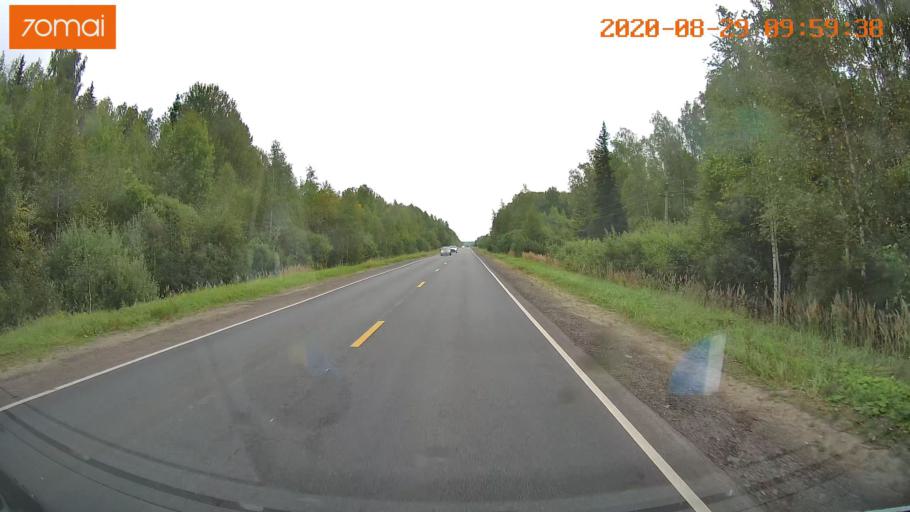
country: RU
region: Ivanovo
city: Zarechnyy
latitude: 57.4108
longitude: 42.3714
